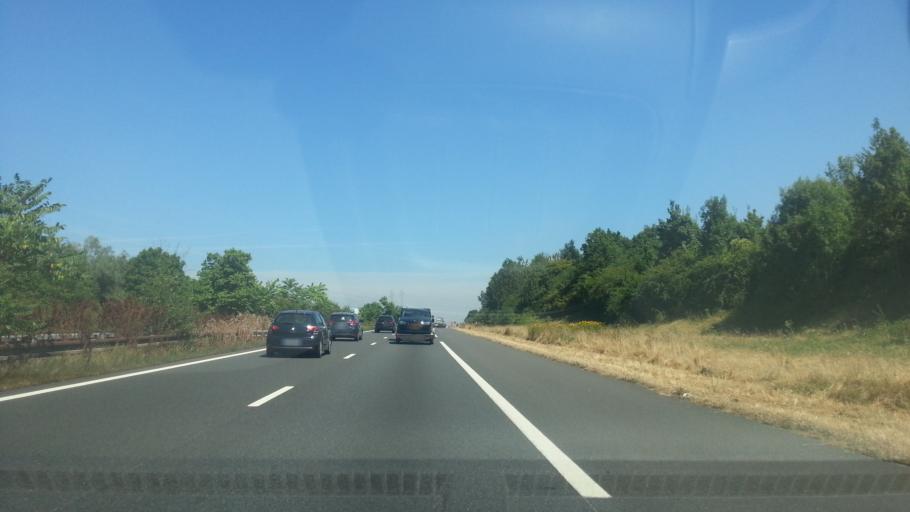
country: FR
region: Ile-de-France
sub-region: Departement de l'Essonne
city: Orsay
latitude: 48.6722
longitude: 2.1966
